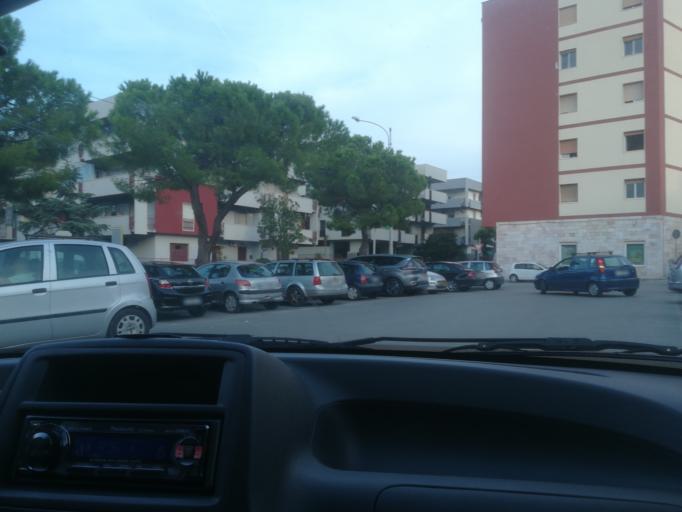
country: IT
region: Apulia
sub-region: Provincia di Bari
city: Monopoli
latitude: 40.9464
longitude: 17.3041
